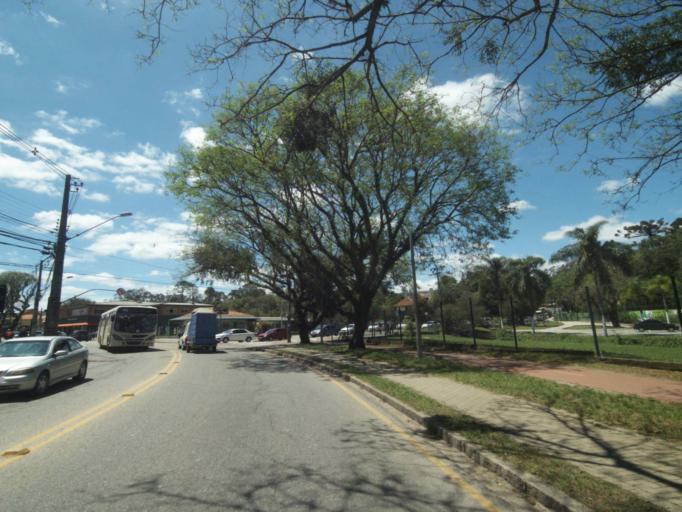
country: BR
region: Parana
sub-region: Curitiba
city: Curitiba
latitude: -25.3917
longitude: -49.2676
